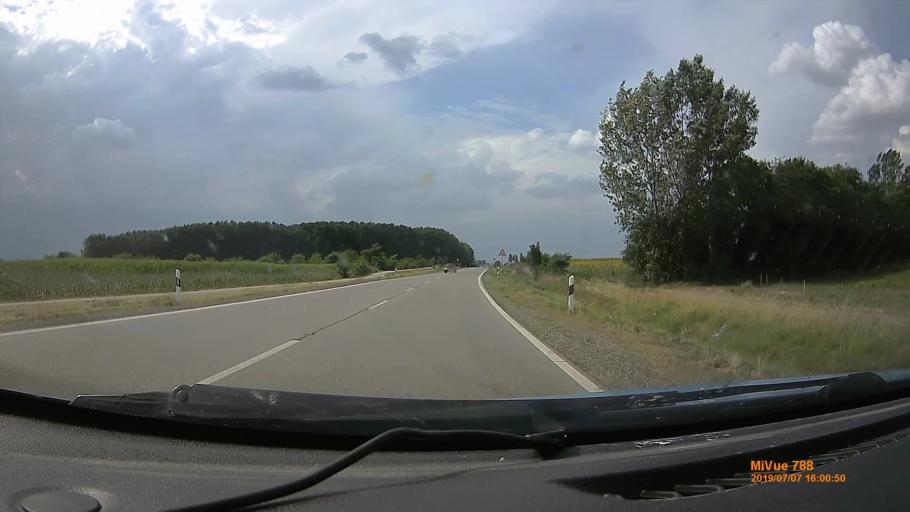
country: HU
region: Heves
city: Boldog
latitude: 47.6025
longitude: 19.7435
